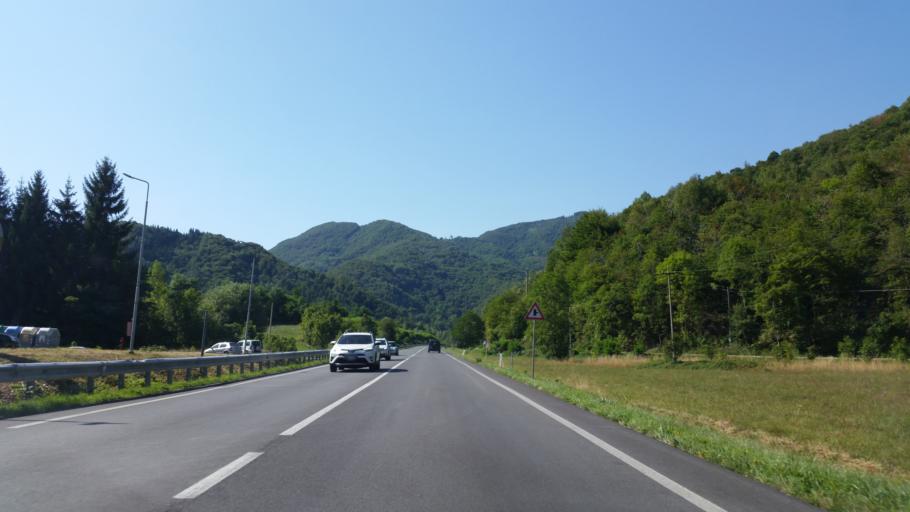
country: IT
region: Piedmont
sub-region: Provincia di Cuneo
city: Robilante
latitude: 44.2711
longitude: 7.5190
